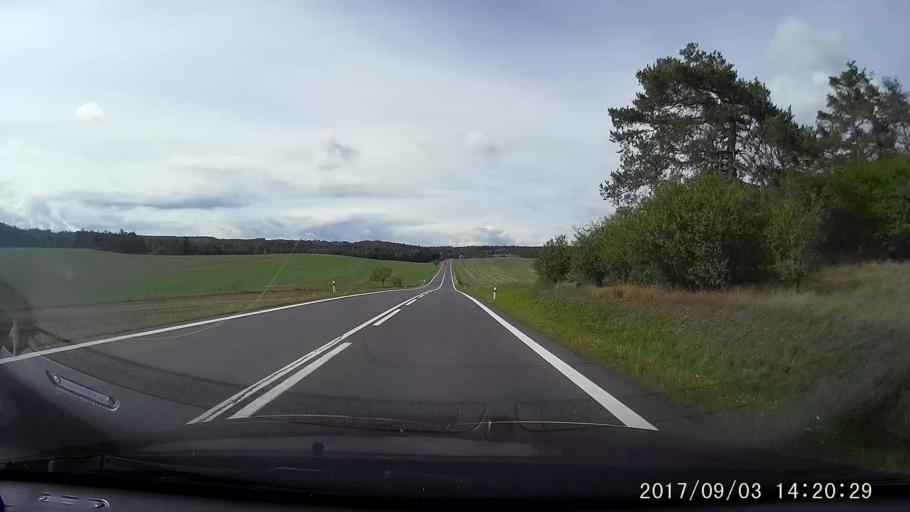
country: CZ
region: South Moravian
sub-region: Okres Znojmo
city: Jevisovice
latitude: 48.9334
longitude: 15.9375
